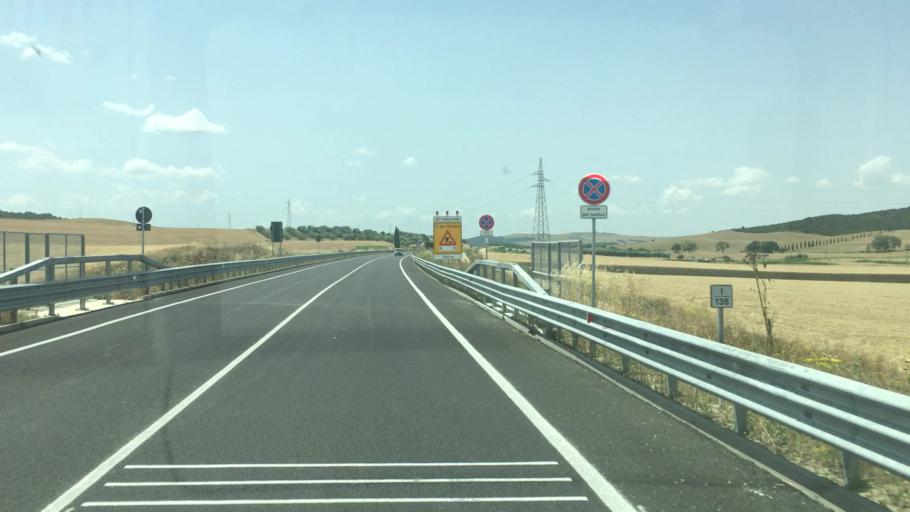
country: IT
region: Basilicate
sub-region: Provincia di Matera
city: La Martella
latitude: 40.6716
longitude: 16.5036
